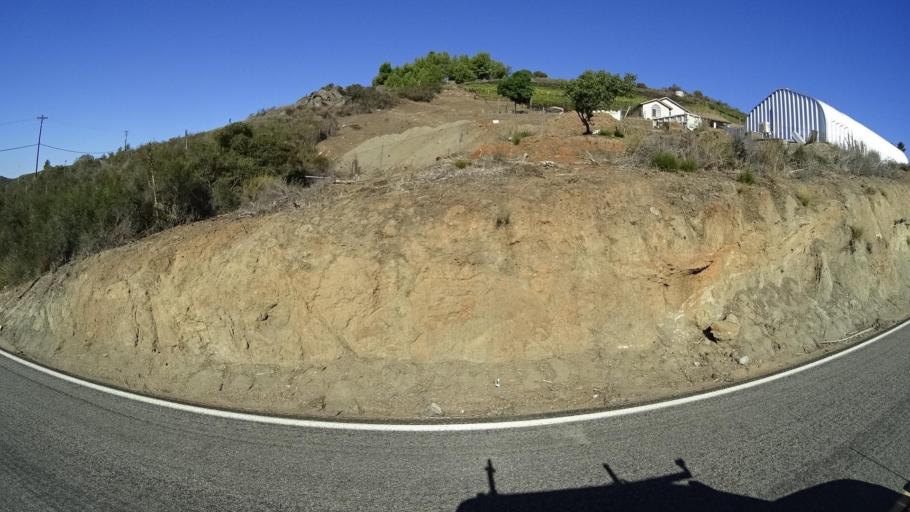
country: US
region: California
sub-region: San Diego County
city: Jamul
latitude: 32.6871
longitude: -116.7499
